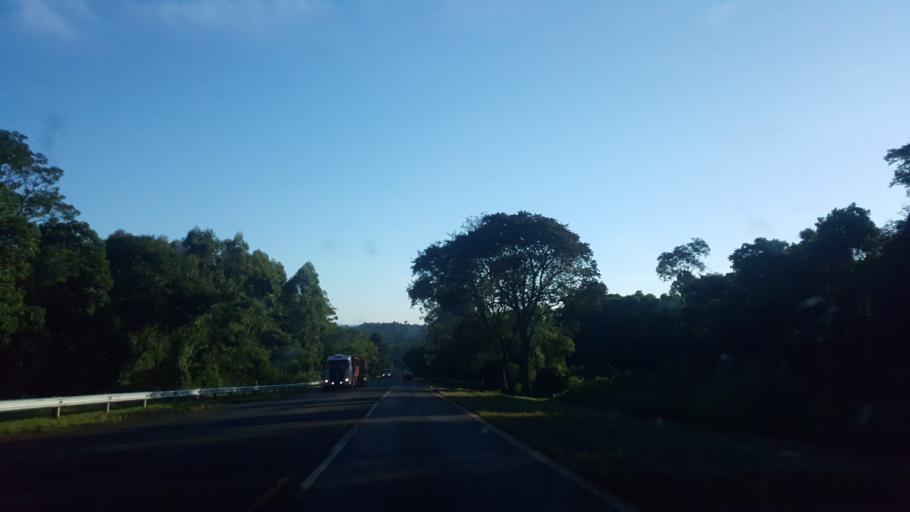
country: AR
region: Misiones
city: El Alcazar
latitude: -26.7285
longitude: -54.8698
